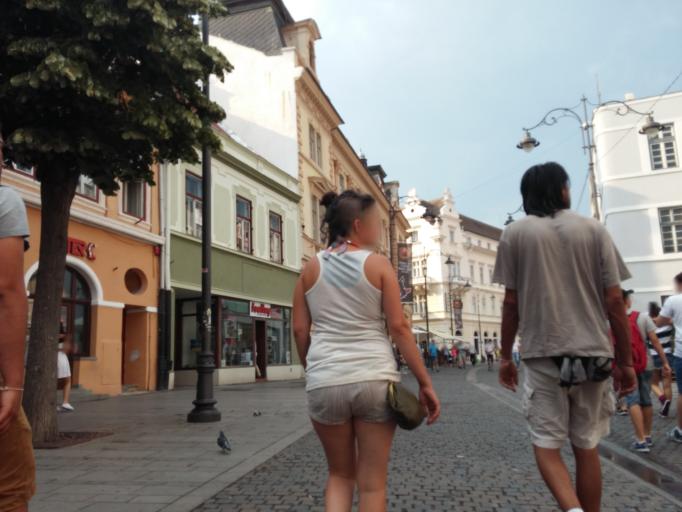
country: RO
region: Sibiu
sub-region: Municipiul Sibiu
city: Sibiu
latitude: 45.7947
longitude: 24.1505
